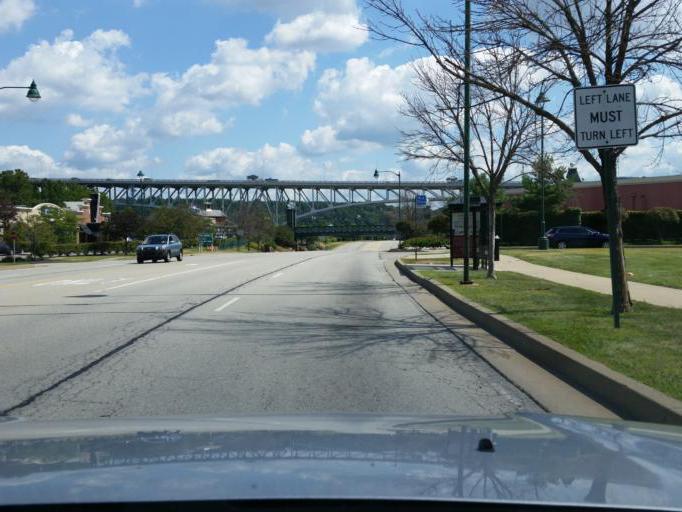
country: US
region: Pennsylvania
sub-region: Allegheny County
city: Homestead
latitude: 40.4074
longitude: -79.9190
